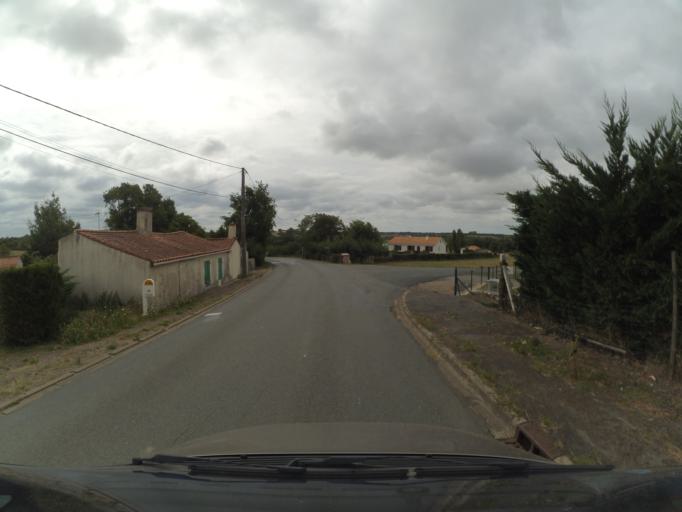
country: FR
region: Pays de la Loire
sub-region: Departement de la Vendee
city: Les Magnils-Reigniers
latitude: 46.4445
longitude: -1.2682
